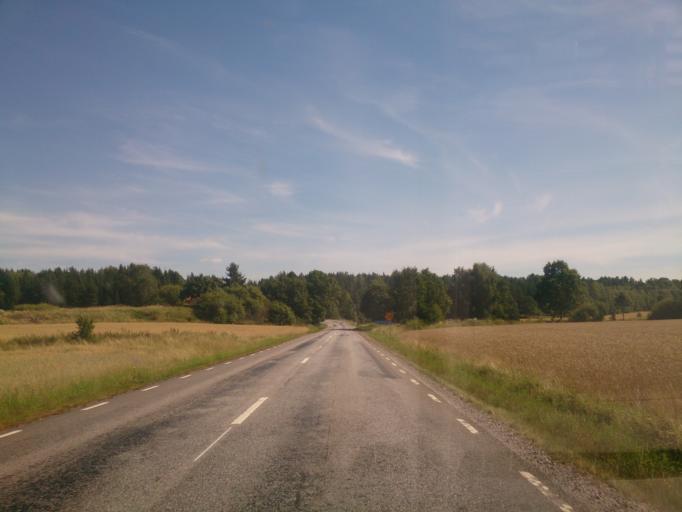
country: SE
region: OEstergoetland
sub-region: Norrkopings Kommun
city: Norrkoping
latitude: 58.4923
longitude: 16.1312
